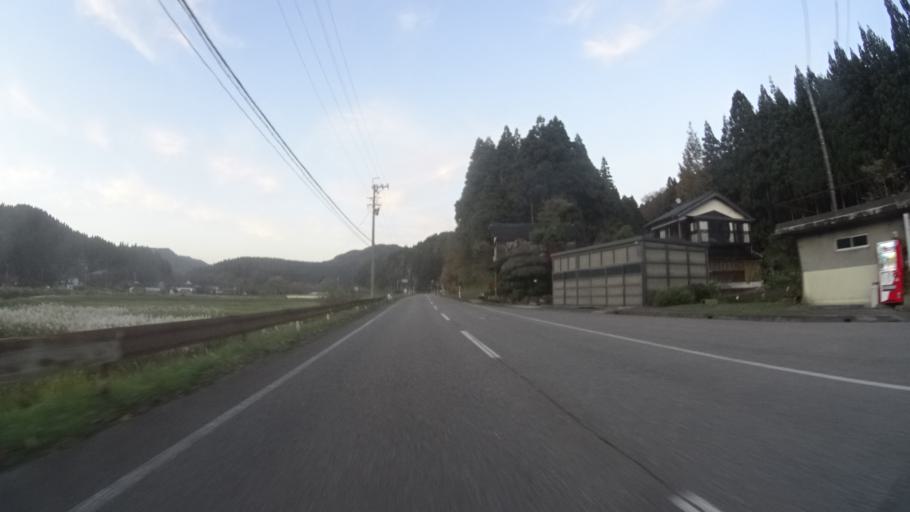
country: JP
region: Ishikawa
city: Nanao
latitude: 37.3028
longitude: 136.7987
